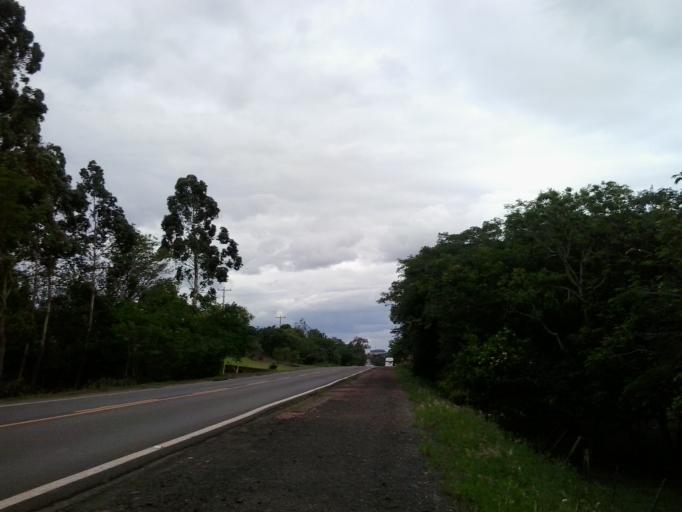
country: BR
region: Rio Grande do Sul
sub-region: Santa Maria
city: Santa Maria
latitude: -29.7323
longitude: -53.5407
